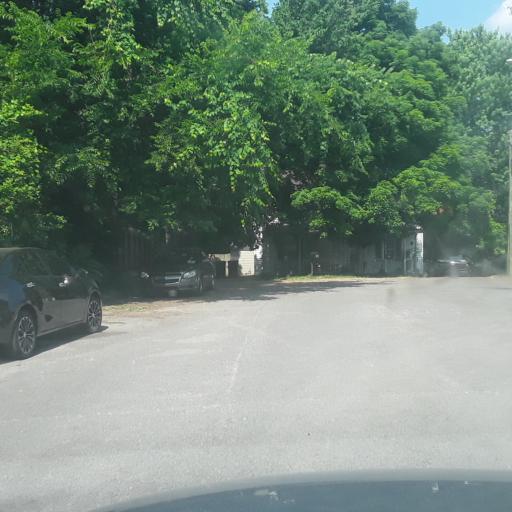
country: US
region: Tennessee
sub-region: Williamson County
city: Brentwood Estates
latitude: 36.0338
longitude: -86.7092
